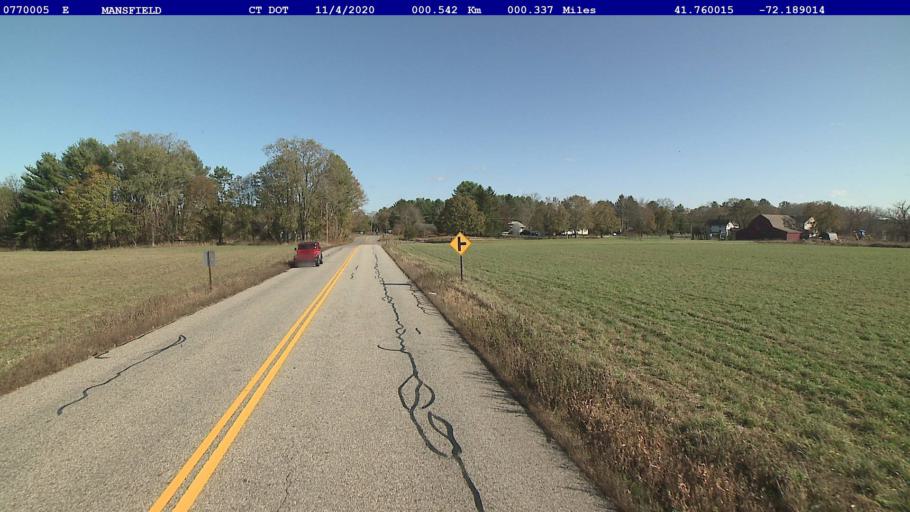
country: US
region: Connecticut
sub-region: Tolland County
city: Mansfield City
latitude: 41.7600
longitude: -72.1890
